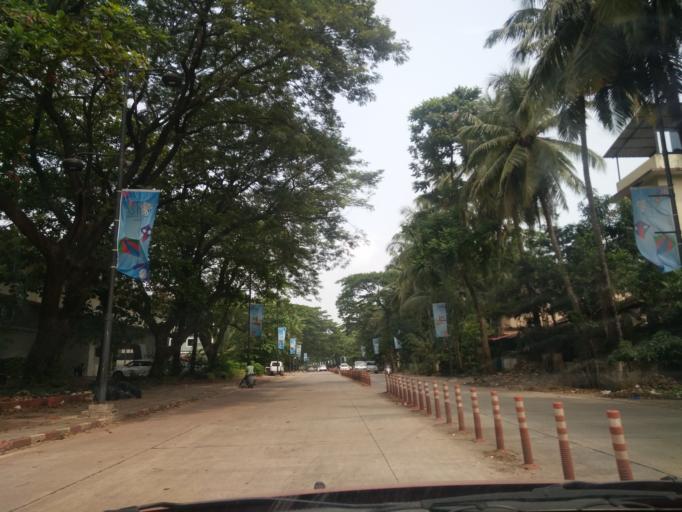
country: IN
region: Goa
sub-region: North Goa
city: Taleigao
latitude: 15.4663
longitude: 73.8065
